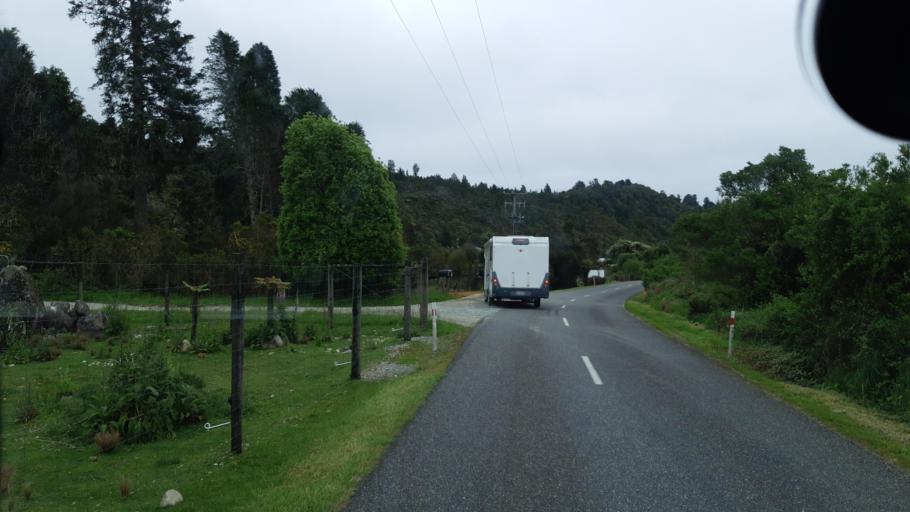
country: NZ
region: West Coast
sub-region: Grey District
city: Greymouth
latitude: -42.6358
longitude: 171.2759
